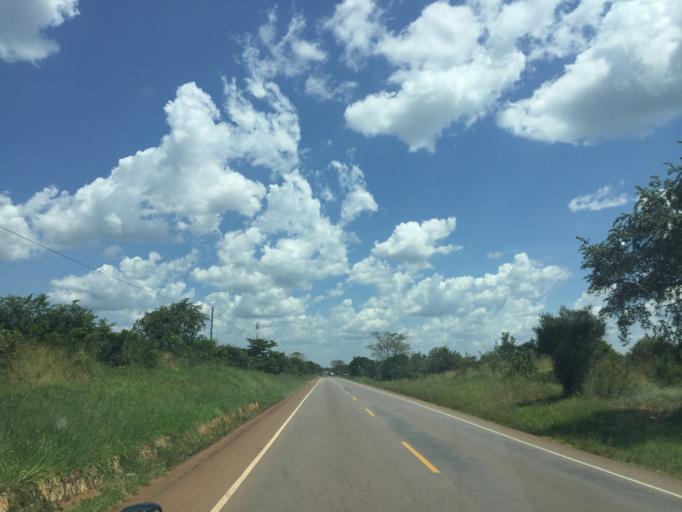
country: UG
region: Central Region
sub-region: Nakasongola District
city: Nakasongola
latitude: 1.3619
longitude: 32.3662
